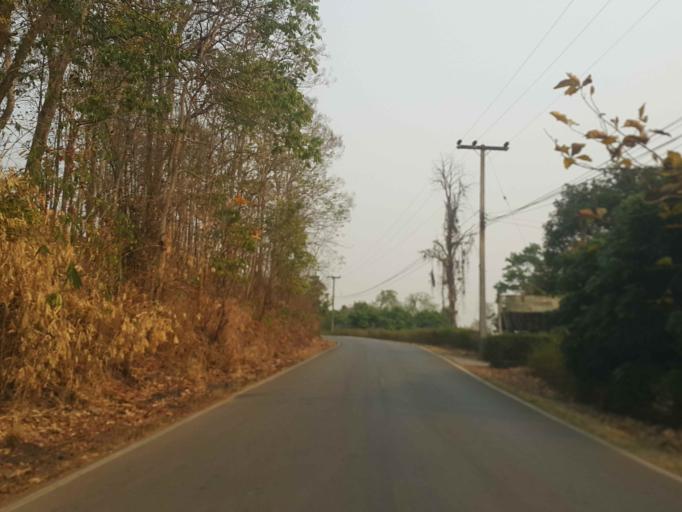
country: TH
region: Chiang Mai
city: Mae Taeng
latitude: 19.1111
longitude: 98.8965
